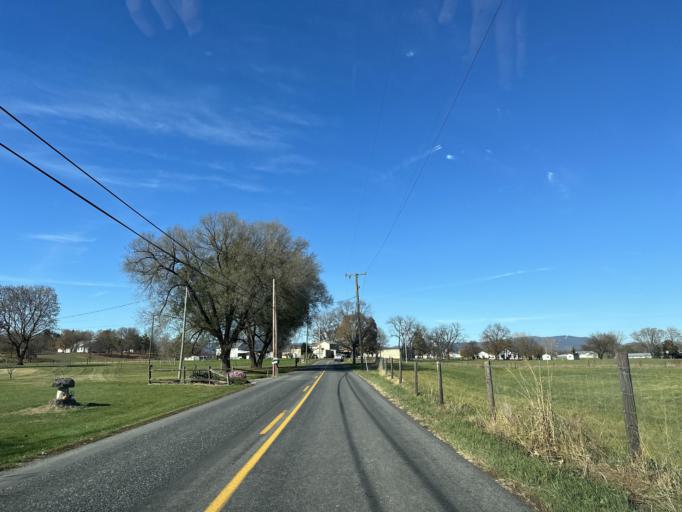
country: US
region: Virginia
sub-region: Rockingham County
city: Bridgewater
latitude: 38.4179
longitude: -78.9852
